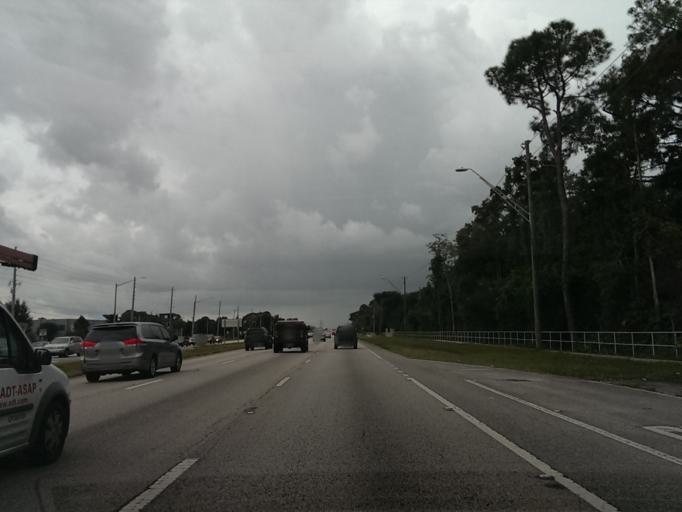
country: US
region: Florida
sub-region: Orange County
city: Orlovista
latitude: 28.5040
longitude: -81.4592
